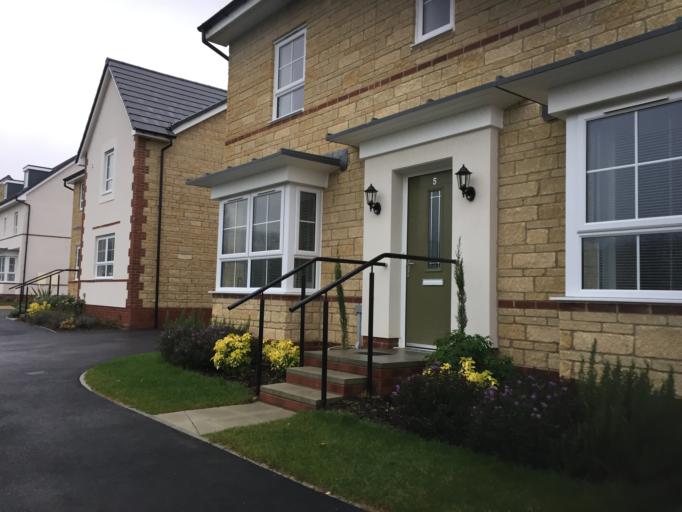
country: GB
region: England
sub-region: Gloucestershire
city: Stonehouse
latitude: 51.7284
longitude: -2.2800
